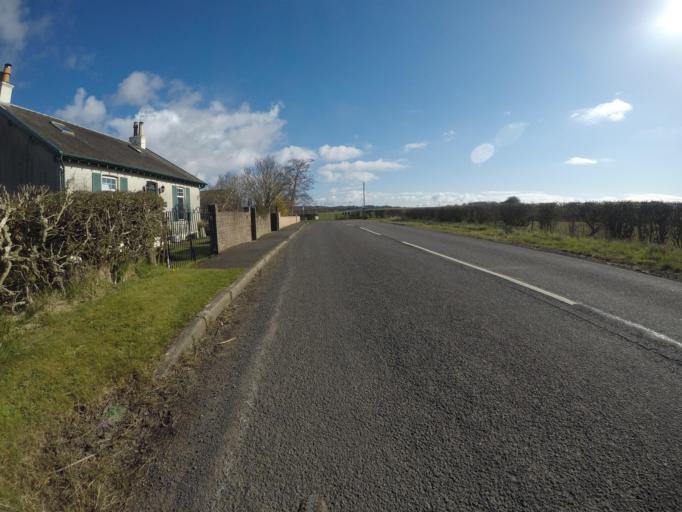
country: GB
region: Scotland
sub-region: North Ayrshire
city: Irvine
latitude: 55.6540
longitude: -4.6528
